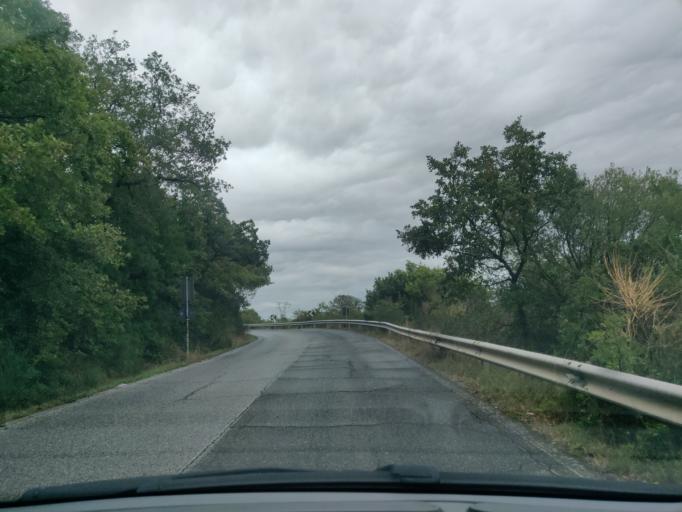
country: IT
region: Latium
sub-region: Citta metropolitana di Roma Capitale
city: Allumiere
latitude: 42.1294
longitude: 11.8518
